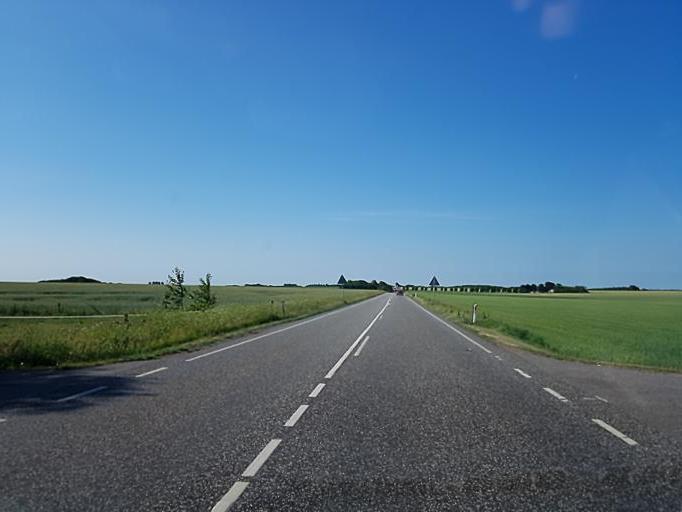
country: DK
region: Central Jutland
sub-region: Ringkobing-Skjern Kommune
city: Skjern
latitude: 56.0448
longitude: 8.5036
